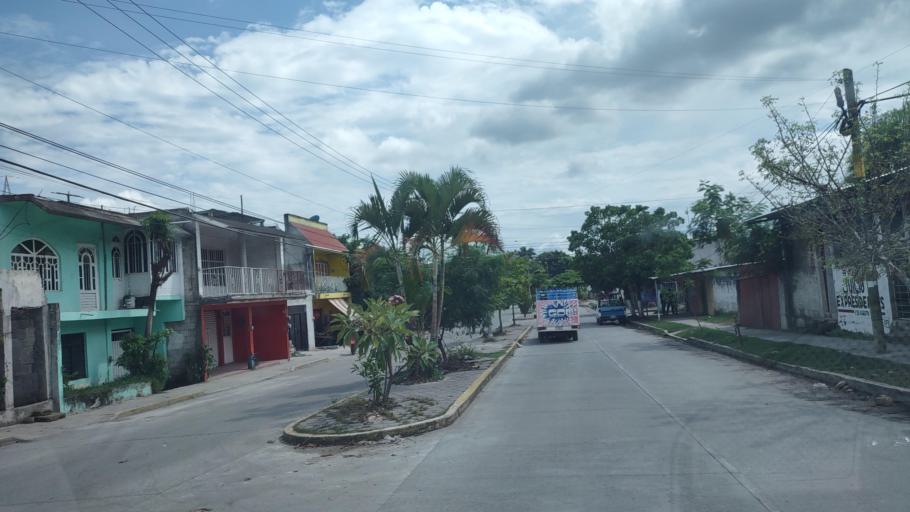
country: MX
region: Veracruz
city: Martinez de la Torre
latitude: 20.0721
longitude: -97.0755
